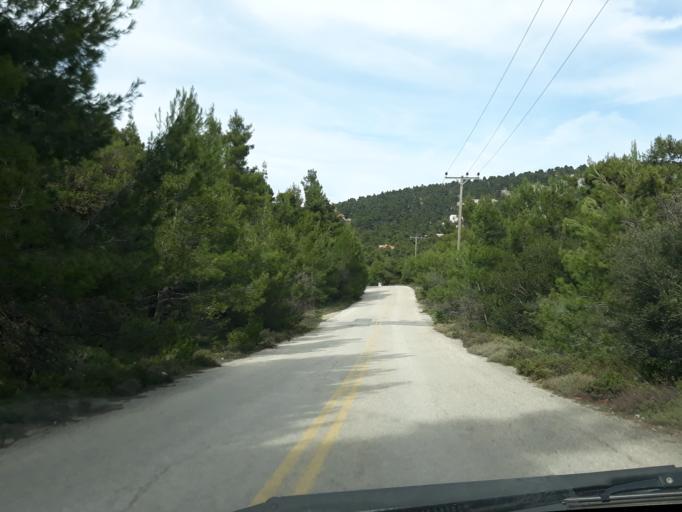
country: GR
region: Attica
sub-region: Nomarchia Anatolikis Attikis
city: Afidnes
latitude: 38.2086
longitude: 23.7995
